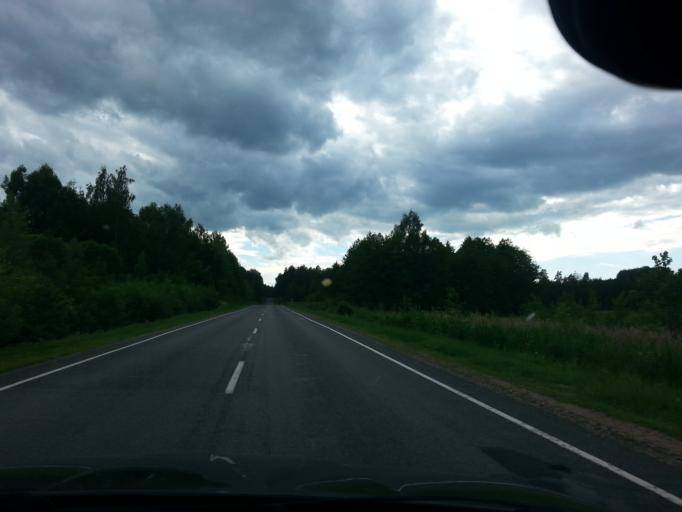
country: BY
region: Minsk
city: Svir
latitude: 54.8541
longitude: 26.2801
